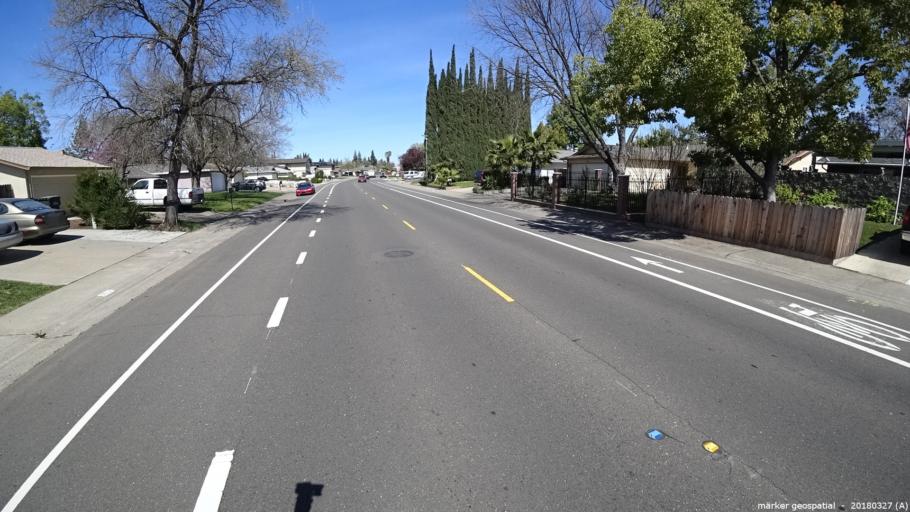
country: US
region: California
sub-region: Sacramento County
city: La Riviera
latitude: 38.5562
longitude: -121.3540
